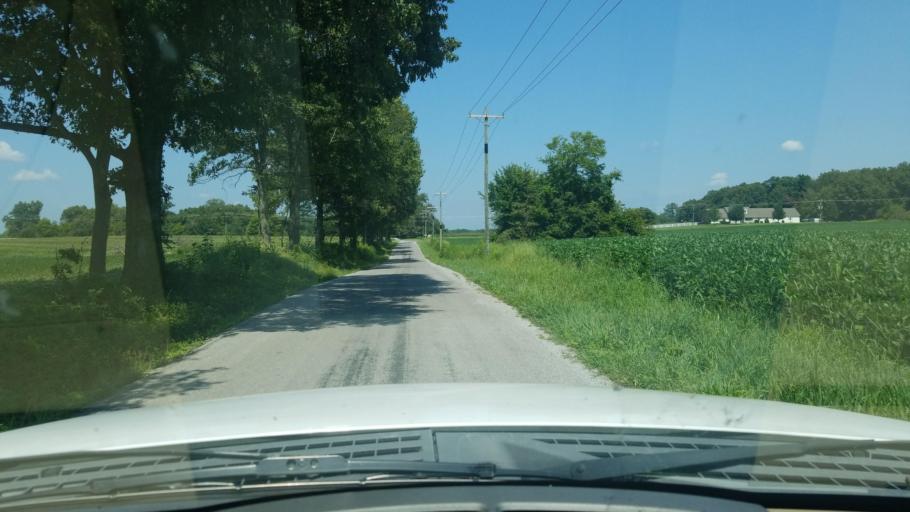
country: US
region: Illinois
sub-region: Saline County
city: Harrisburg
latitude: 37.8026
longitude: -88.6240
